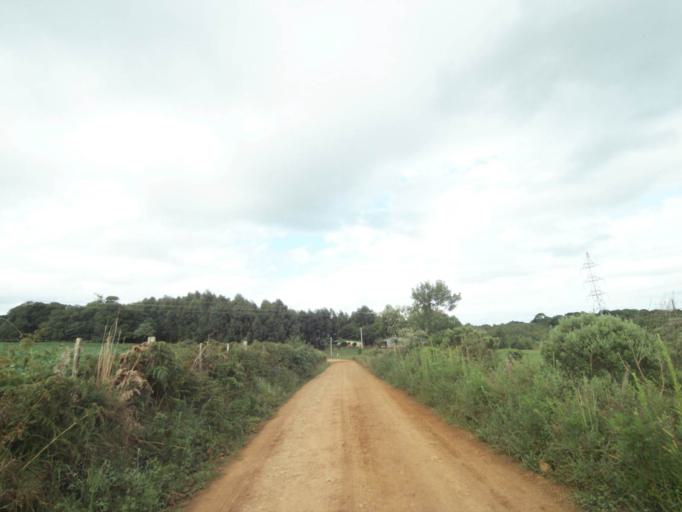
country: BR
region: Rio Grande do Sul
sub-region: Lagoa Vermelha
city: Lagoa Vermelha
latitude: -28.1989
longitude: -51.5121
